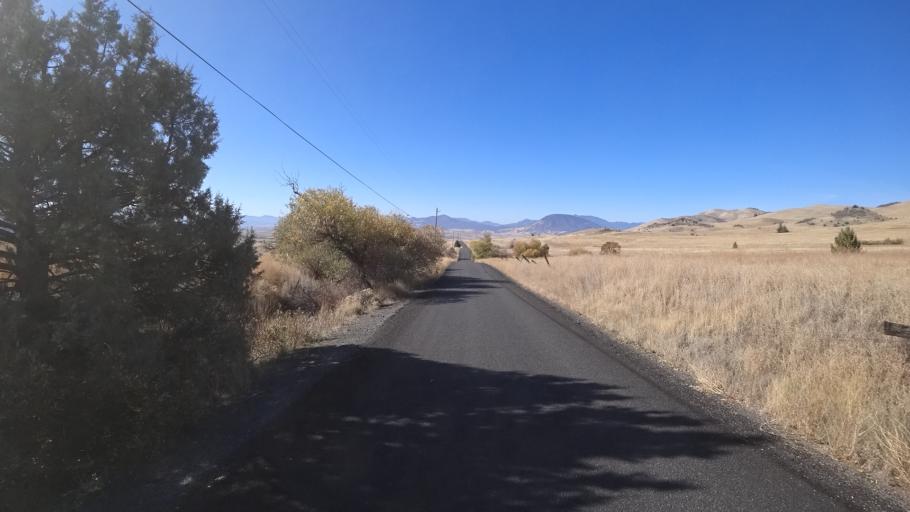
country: US
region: California
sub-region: Siskiyou County
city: Montague
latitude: 41.8304
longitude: -122.3471
